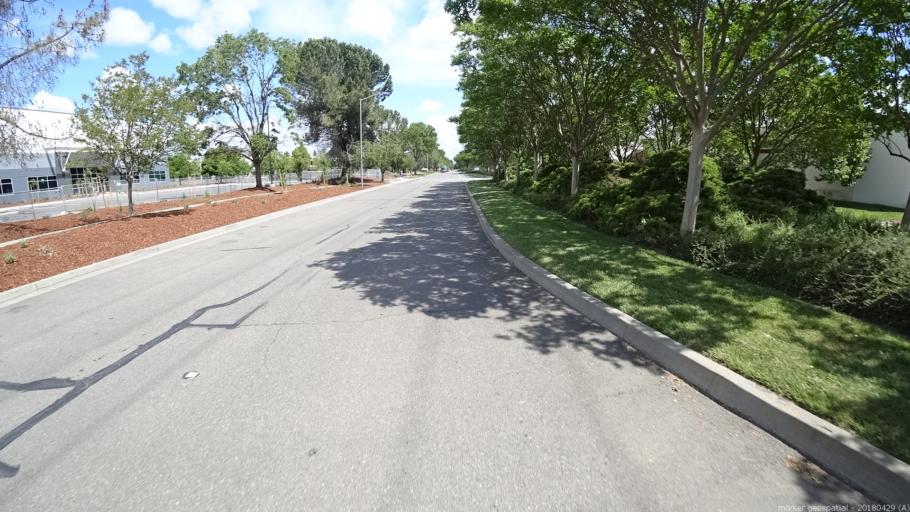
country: US
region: California
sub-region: Yolo County
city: West Sacramento
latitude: 38.5866
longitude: -121.5595
